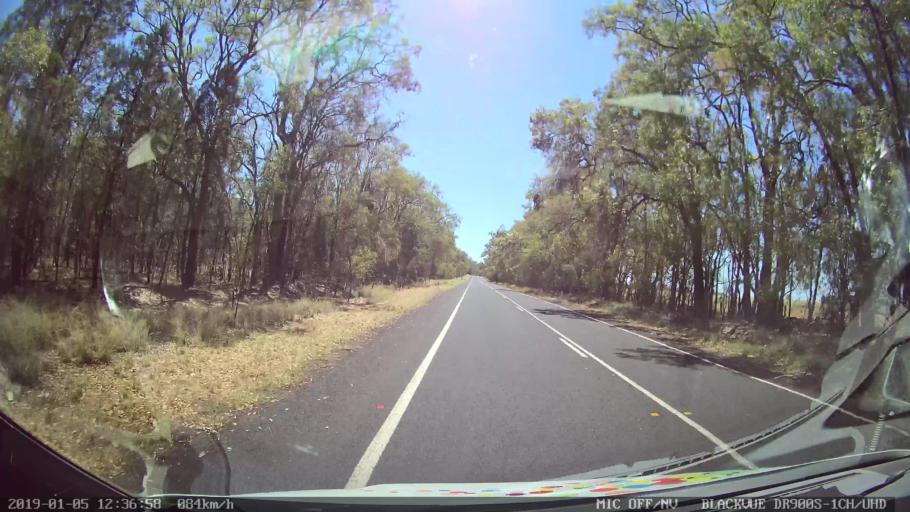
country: AU
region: New South Wales
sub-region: Warrumbungle Shire
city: Coonabarabran
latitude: -31.2057
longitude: 149.4481
